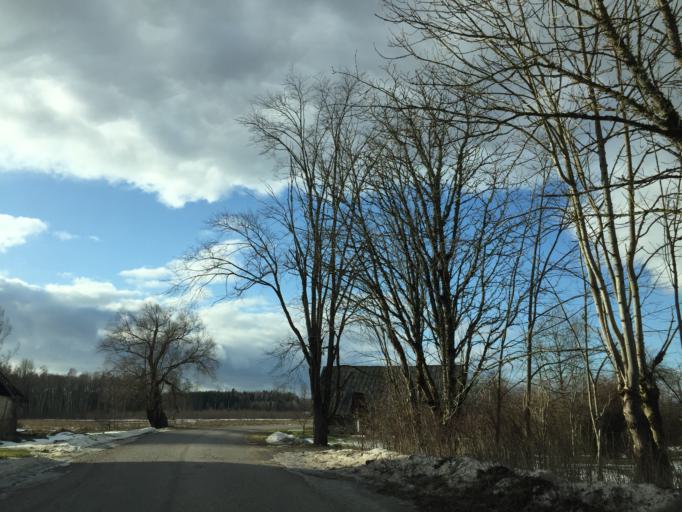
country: LV
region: Limbazu Rajons
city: Limbazi
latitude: 57.6087
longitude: 24.6064
